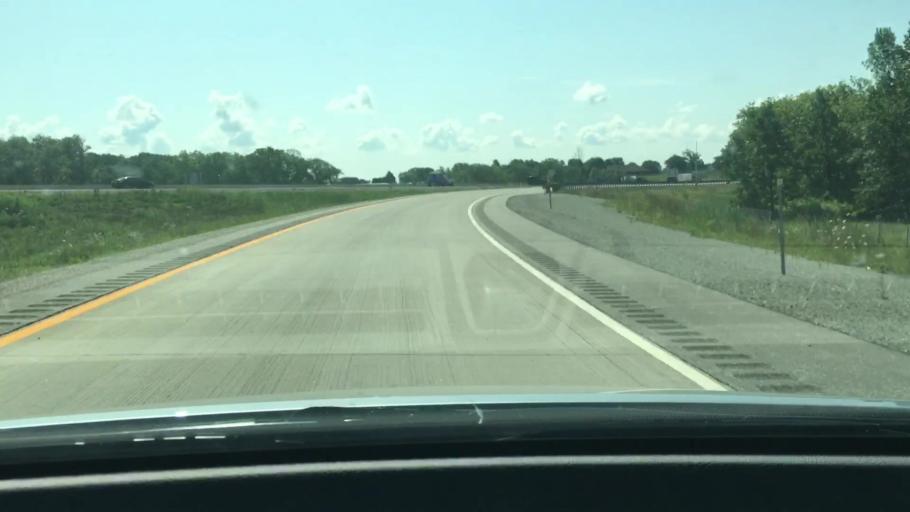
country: US
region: Wisconsin
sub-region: Brown County
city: Ashwaubenon
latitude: 44.4824
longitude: -88.0817
